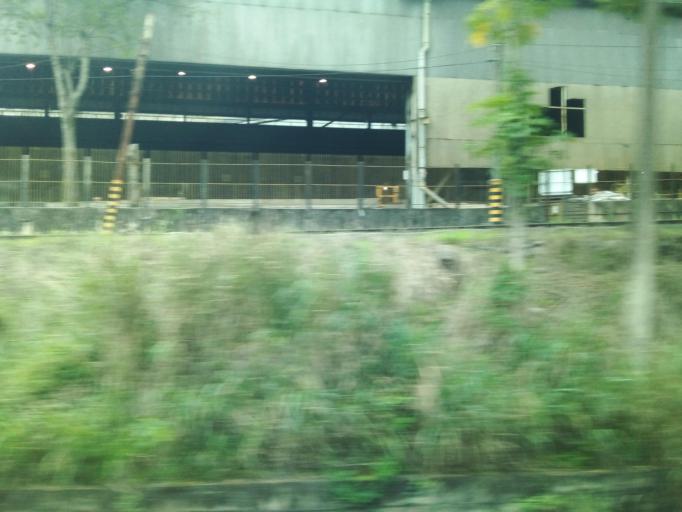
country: BR
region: Minas Gerais
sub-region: Joao Monlevade
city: Joao Monlevade
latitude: -19.8374
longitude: -43.1304
